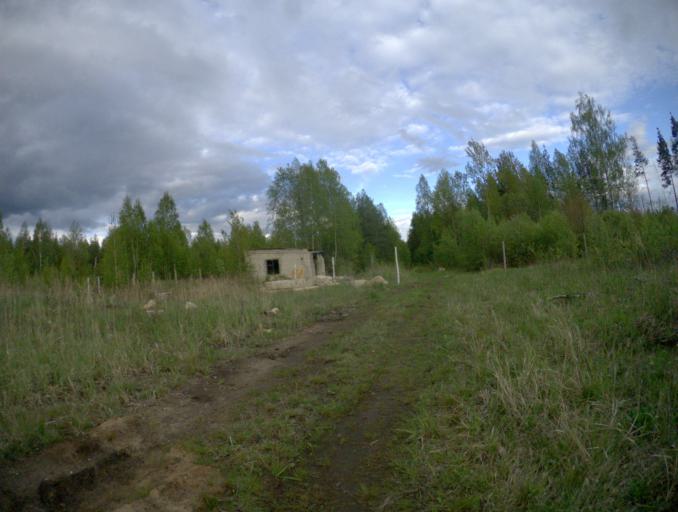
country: RU
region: Vladimir
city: Anopino
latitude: 55.7140
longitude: 40.6048
